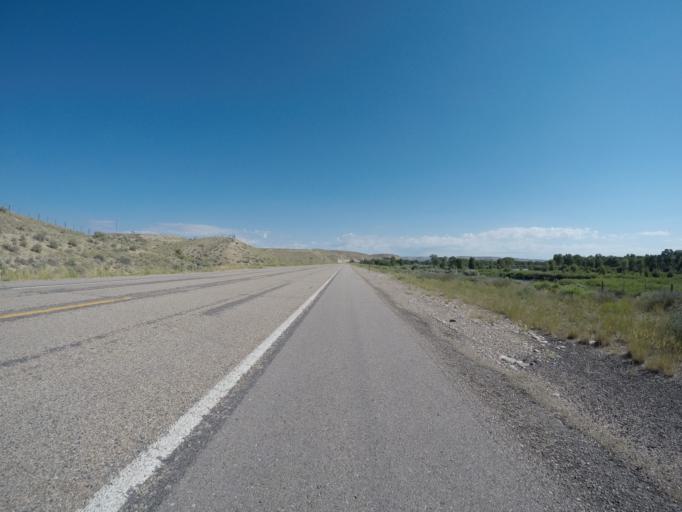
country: US
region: Wyoming
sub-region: Sublette County
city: Marbleton
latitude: 42.1656
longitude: -110.1885
